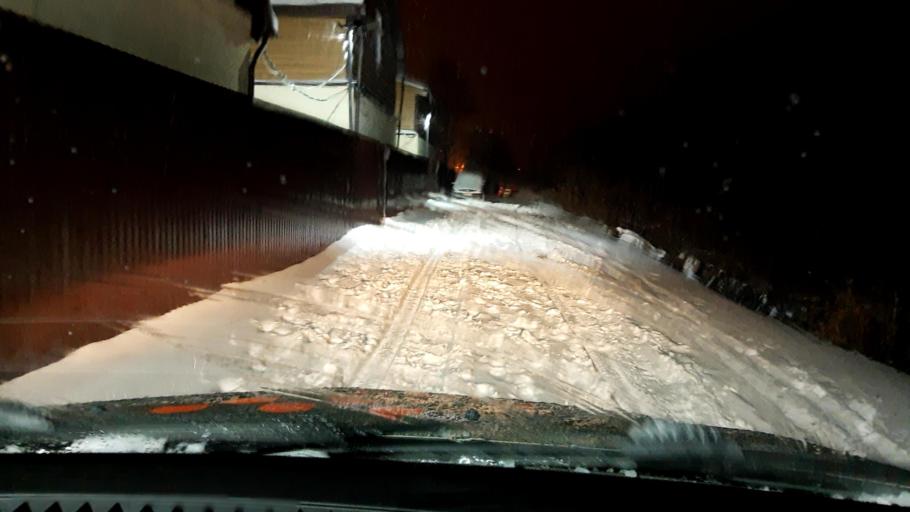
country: RU
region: Bashkortostan
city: Ufa
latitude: 54.7835
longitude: 56.1013
